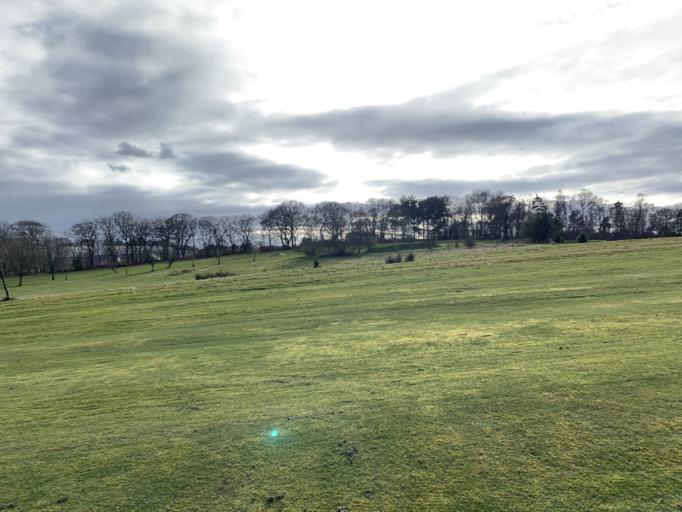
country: GB
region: Scotland
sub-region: East Renfrewshire
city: Newton Mearns
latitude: 55.7934
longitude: -4.3227
